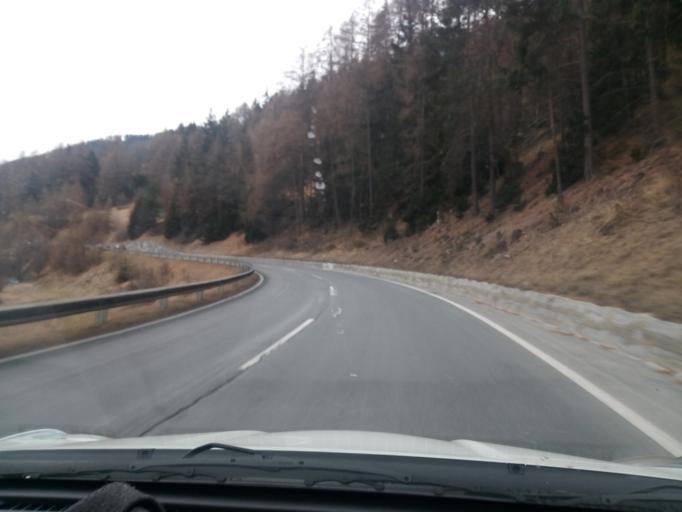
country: AT
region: Tyrol
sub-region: Politischer Bezirk Landeck
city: Nauders
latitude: 46.9028
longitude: 10.4926
